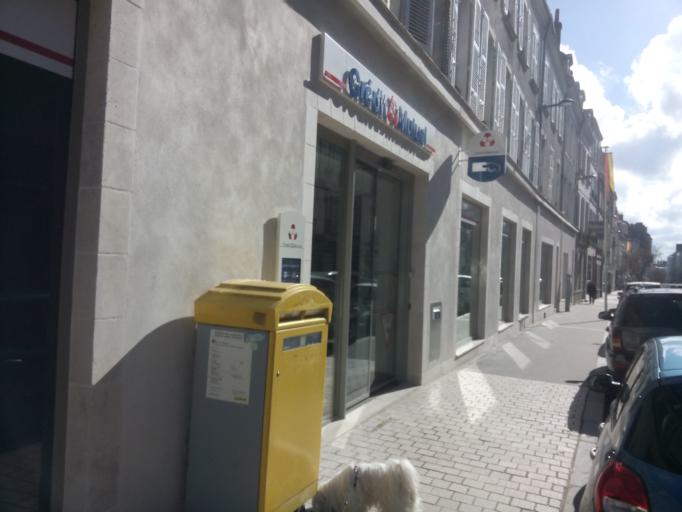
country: FR
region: Centre
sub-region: Departement du Loiret
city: Orleans
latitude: 47.9061
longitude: 1.9022
